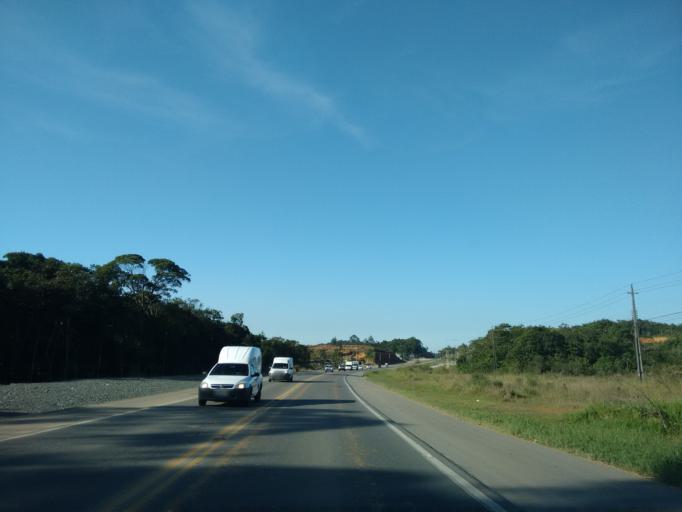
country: BR
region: Santa Catarina
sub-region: Guaramirim
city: Guaramirim
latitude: -26.4546
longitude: -48.9260
